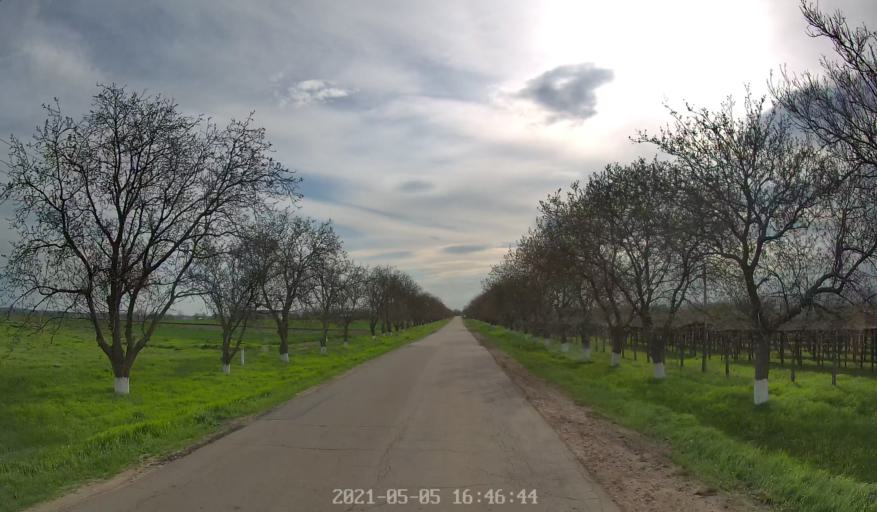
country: MD
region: Chisinau
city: Vadul lui Voda
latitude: 47.0983
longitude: 29.1873
